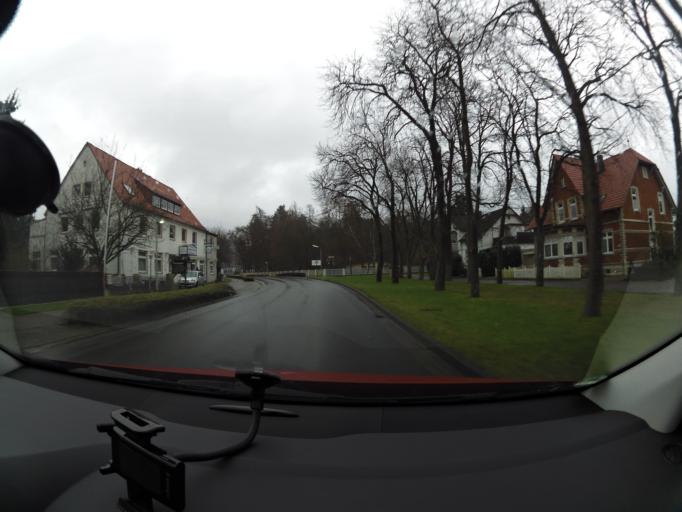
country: DE
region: Lower Saxony
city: Herzberg am Harz
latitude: 51.6600
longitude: 10.3513
